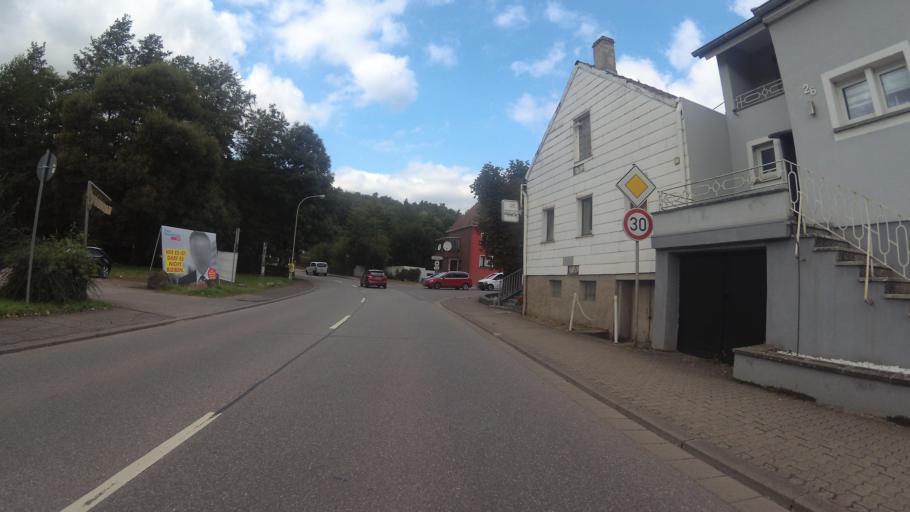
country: DE
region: Saarland
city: Wadgassen
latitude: 49.2490
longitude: 6.7933
